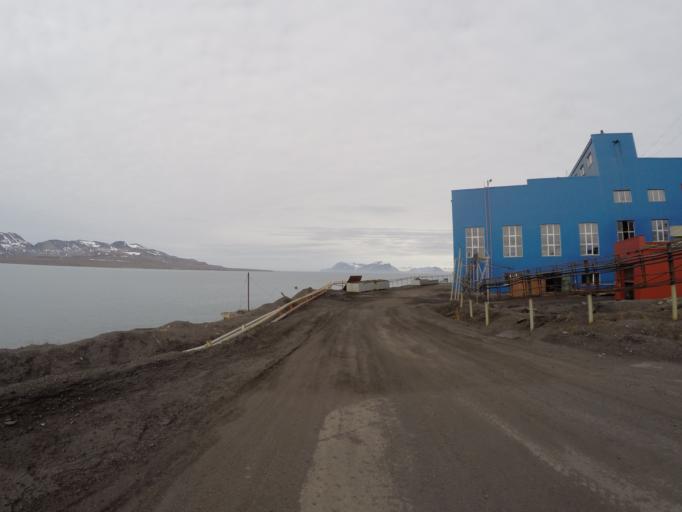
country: SJ
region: Svalbard
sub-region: Spitsbergen
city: Longyearbyen
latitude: 78.0549
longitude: 14.2113
